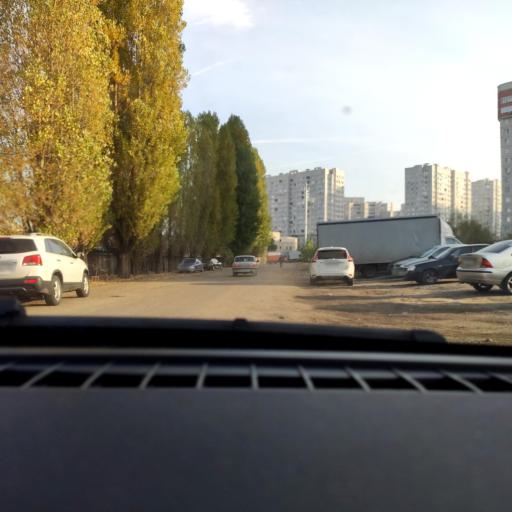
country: RU
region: Voronezj
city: Podgornoye
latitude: 51.7153
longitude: 39.1543
